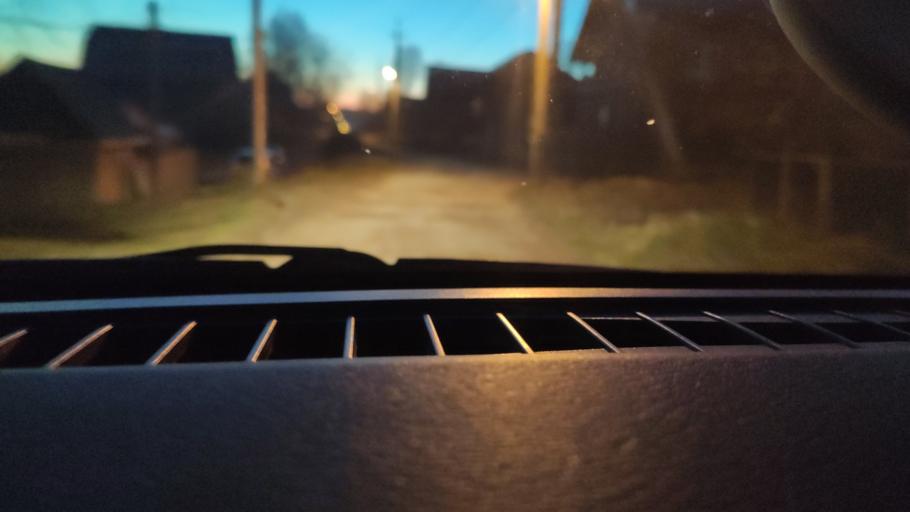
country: RU
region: Perm
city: Perm
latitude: 58.0386
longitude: 56.3394
